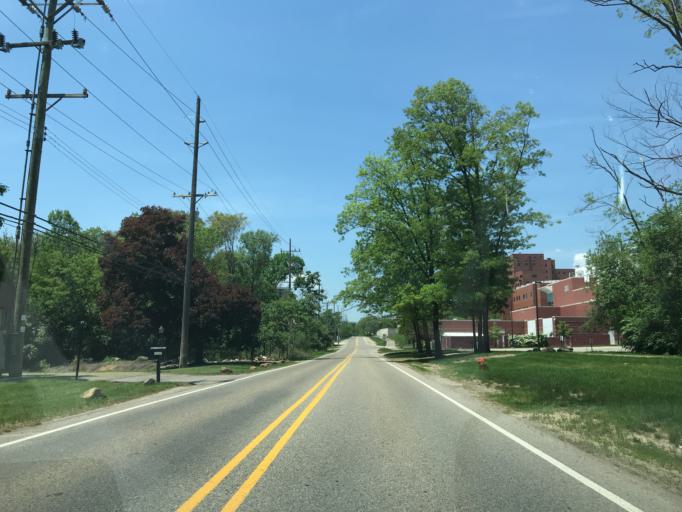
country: US
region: Michigan
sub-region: Washtenaw County
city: Ann Arbor
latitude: 42.2841
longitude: -83.7128
